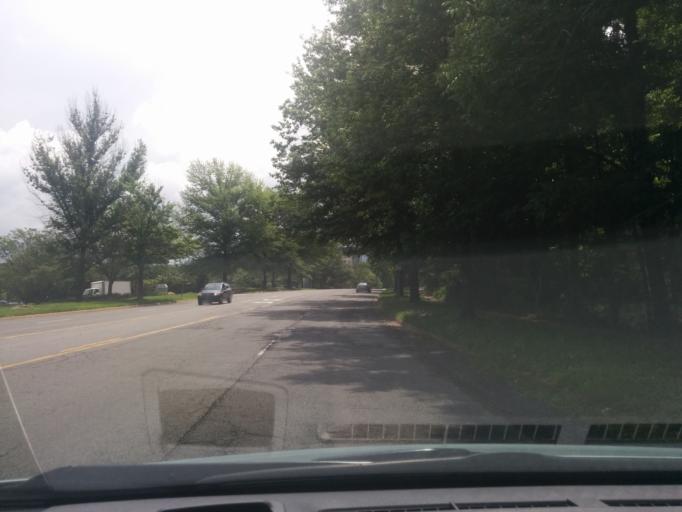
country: US
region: Virginia
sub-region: Fairfax County
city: Tysons Corner
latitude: 38.9283
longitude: -77.2237
